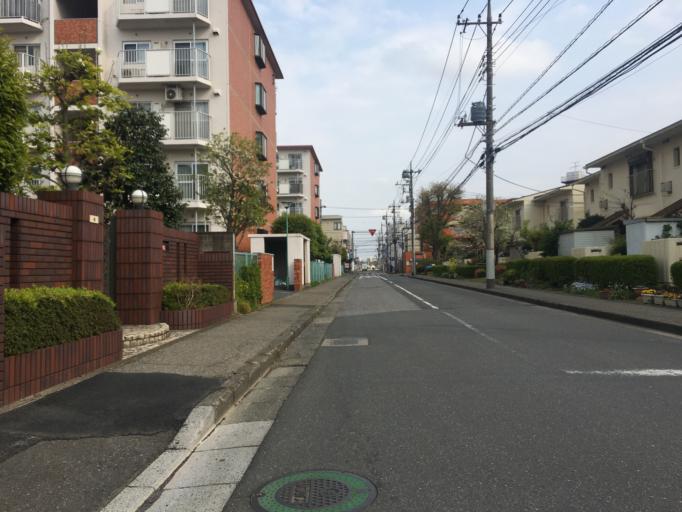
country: JP
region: Saitama
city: Oi
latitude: 35.8365
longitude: 139.5474
